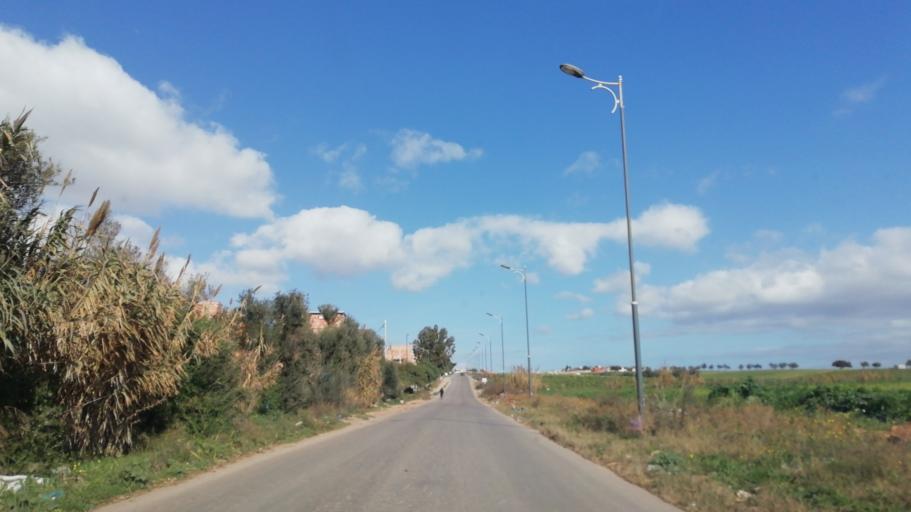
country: DZ
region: Oran
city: Es Senia
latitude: 35.6281
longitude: -0.6616
